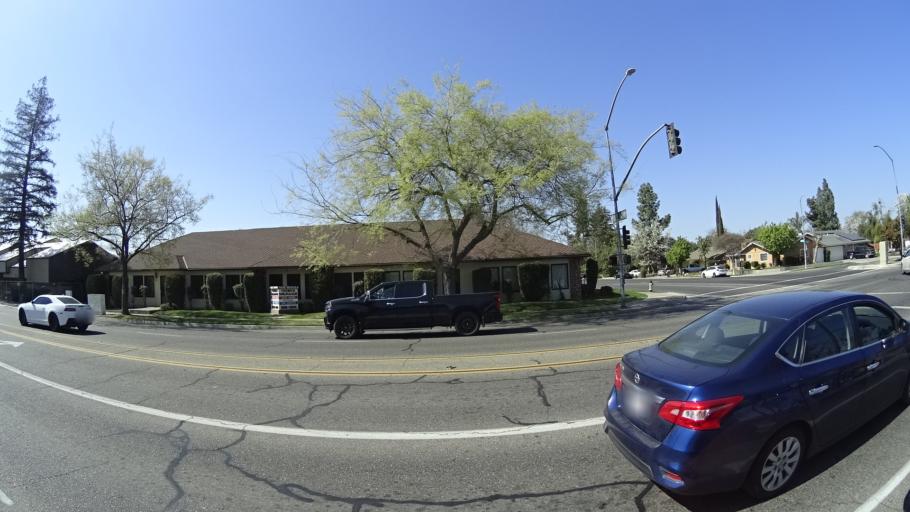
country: US
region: California
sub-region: Fresno County
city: Fresno
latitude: 36.7963
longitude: -119.8264
